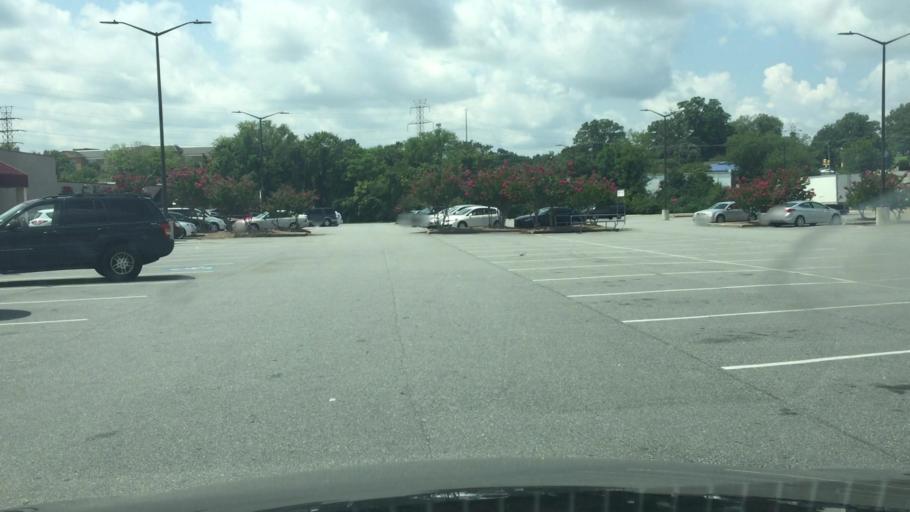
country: US
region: North Carolina
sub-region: Cabarrus County
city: Kannapolis
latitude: 35.4507
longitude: -80.6063
